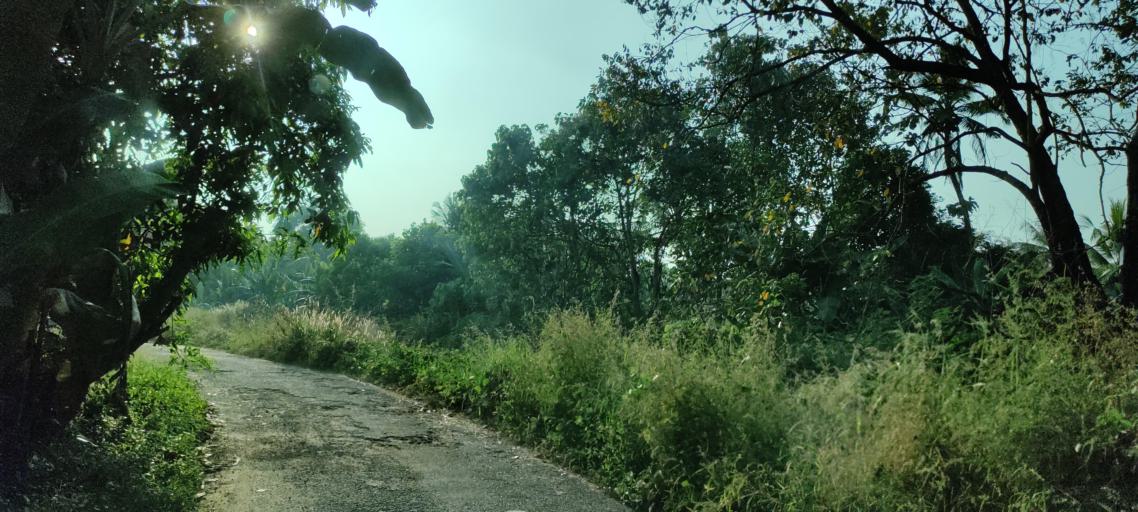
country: IN
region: Kerala
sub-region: Pattanamtitta
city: Adur
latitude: 9.1362
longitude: 76.7298
